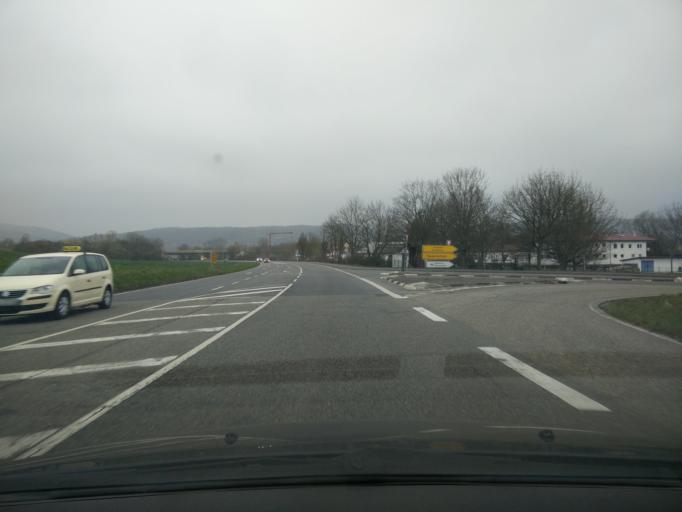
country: DE
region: Rheinland-Pfalz
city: Kapellen-Drusweiler
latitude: 49.1020
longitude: 8.0225
